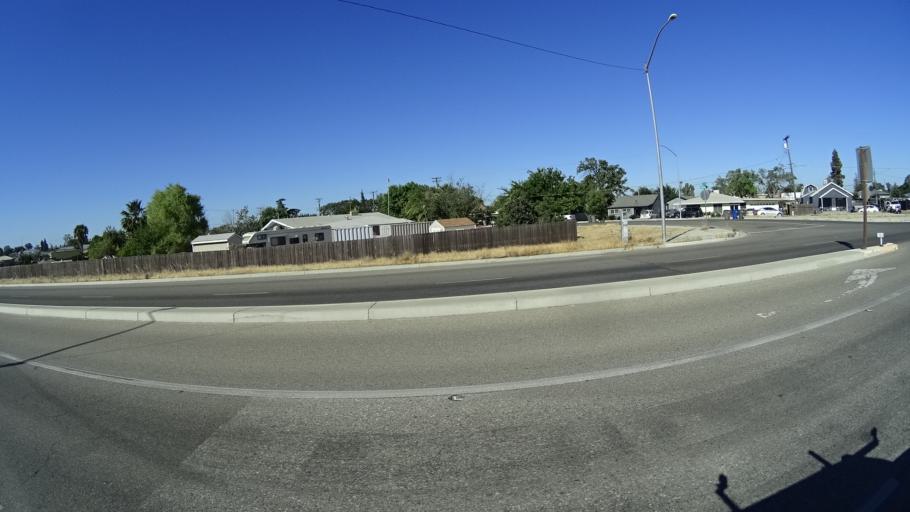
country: US
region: California
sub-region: Fresno County
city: West Park
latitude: 36.7406
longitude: -119.8351
